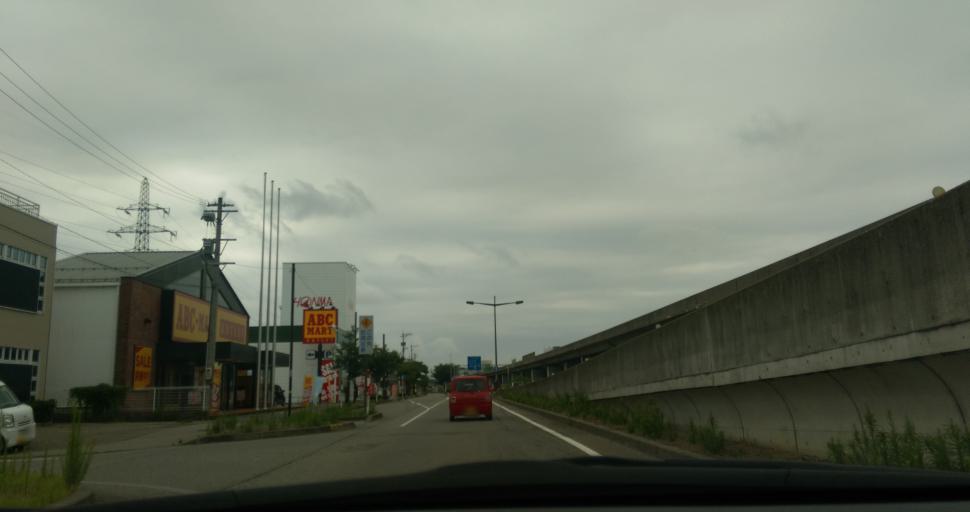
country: JP
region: Ishikawa
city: Kanazawa-shi
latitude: 36.5902
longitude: 136.6297
